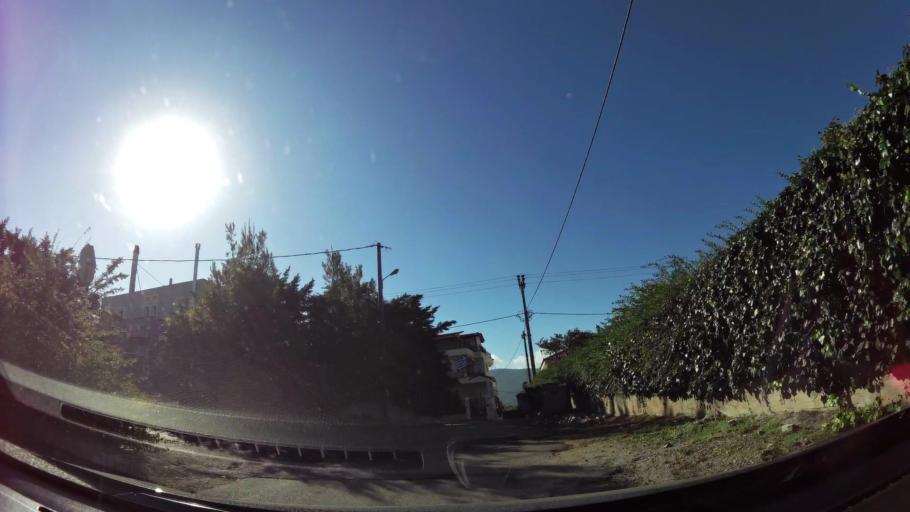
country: GR
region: Attica
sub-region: Nomarchia Anatolikis Attikis
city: Anoixi
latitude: 38.1336
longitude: 23.8658
